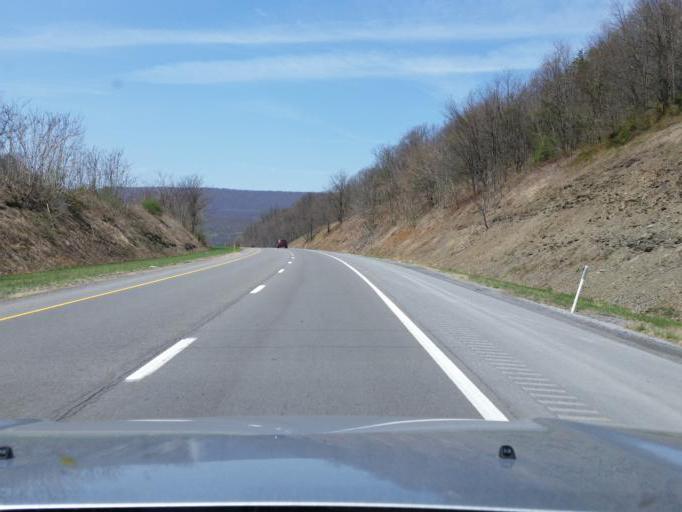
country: US
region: Pennsylvania
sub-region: Juniata County
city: Mifflintown
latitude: 40.5940
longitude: -77.3771
